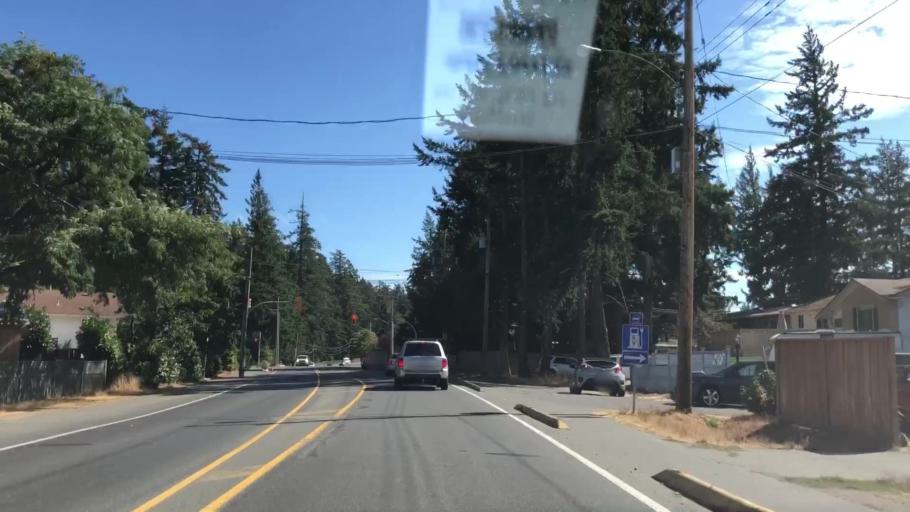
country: CA
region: British Columbia
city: Colwood
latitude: 48.4270
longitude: -123.4914
